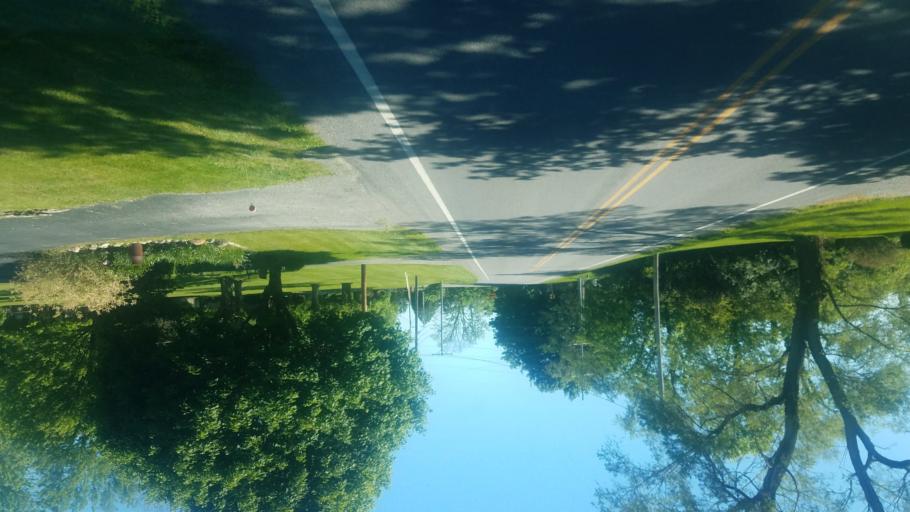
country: US
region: Ohio
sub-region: Logan County
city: Bellefontaine
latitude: 40.3761
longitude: -83.7805
